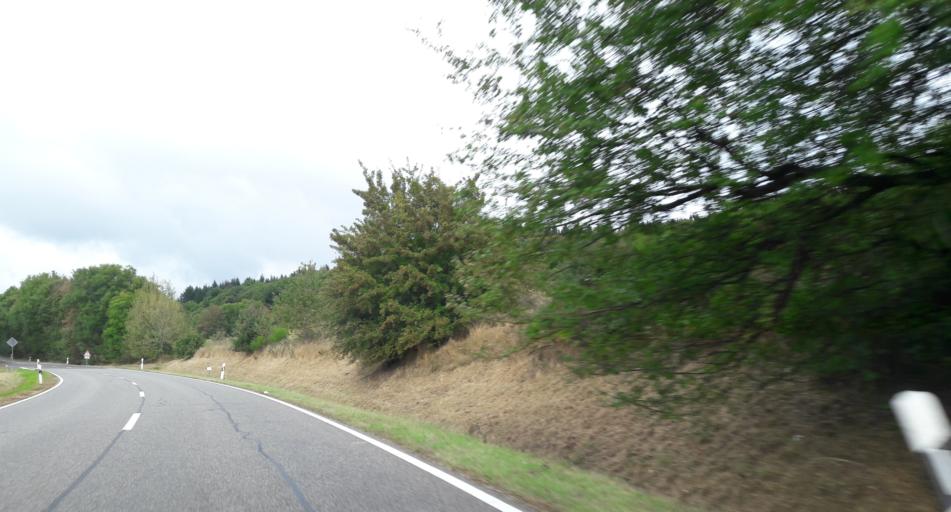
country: DE
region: Saarland
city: Freisen
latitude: 49.5293
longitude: 7.2275
